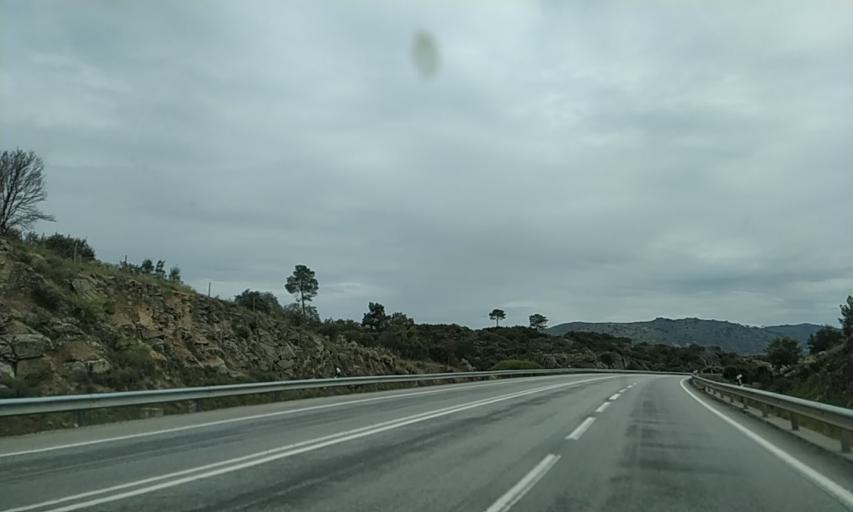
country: PT
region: Guarda
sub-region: Celorico da Beira
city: Celorico da Beira
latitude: 40.6307
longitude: -7.3105
